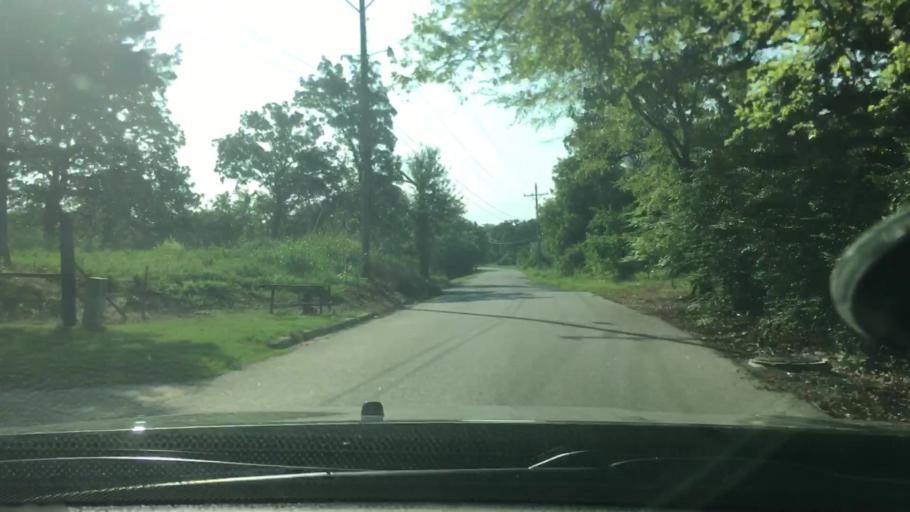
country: US
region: Oklahoma
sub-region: Atoka County
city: Atoka
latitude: 34.3908
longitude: -96.1338
